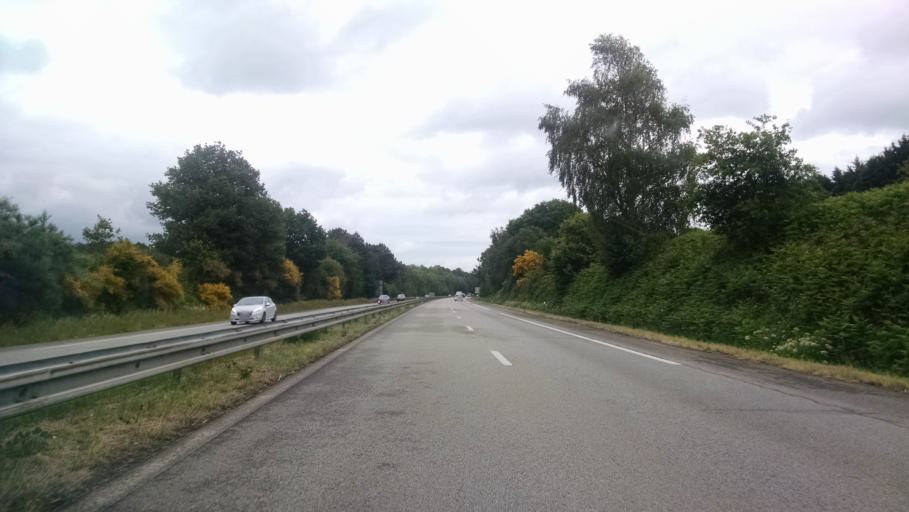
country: FR
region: Brittany
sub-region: Departement du Morbihan
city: Kervignac
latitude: 47.7864
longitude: -3.2248
